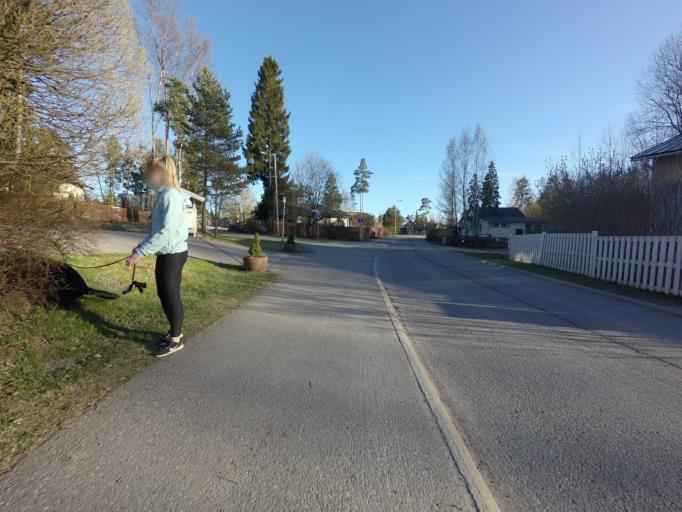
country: FI
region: Uusimaa
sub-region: Helsinki
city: Espoo
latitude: 60.1641
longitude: 24.6722
